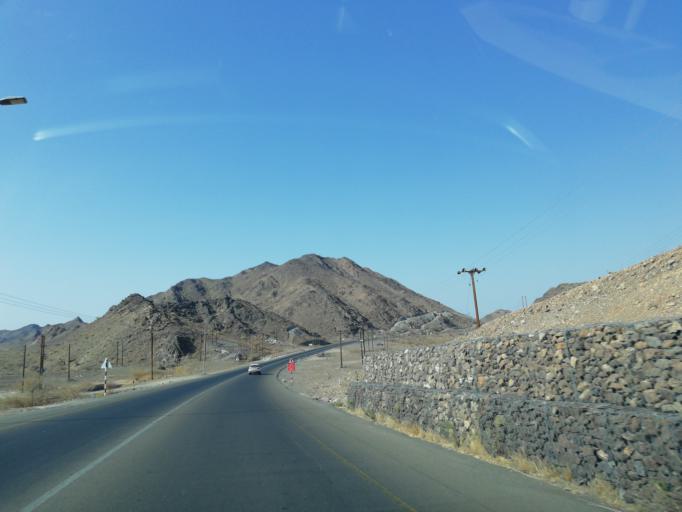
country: OM
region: Ash Sharqiyah
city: Ibra'
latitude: 22.8096
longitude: 58.1689
